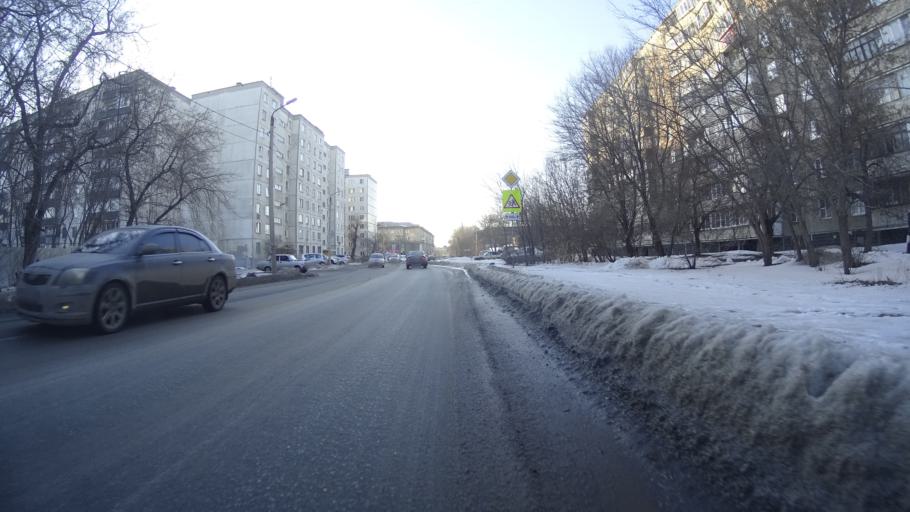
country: RU
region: Chelyabinsk
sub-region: Gorod Chelyabinsk
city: Chelyabinsk
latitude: 55.1382
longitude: 61.4460
